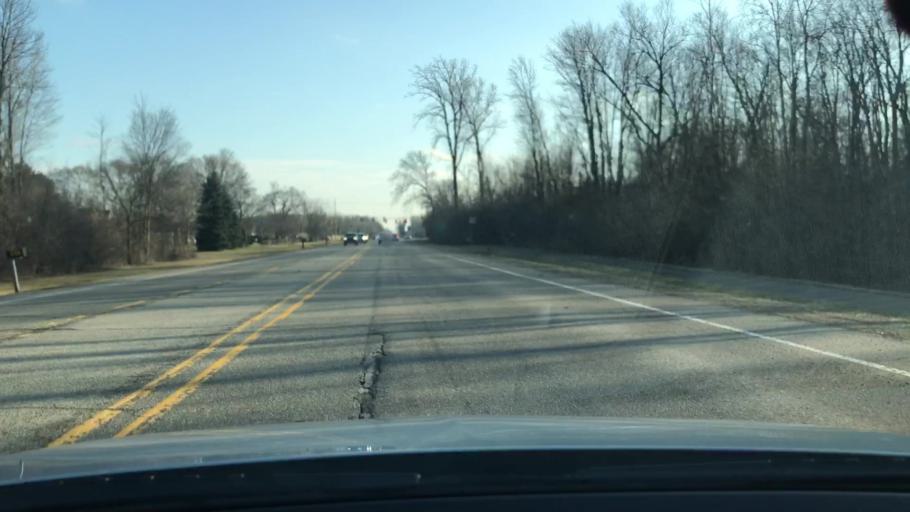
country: US
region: Michigan
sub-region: Oakland County
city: Rochester
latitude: 42.6555
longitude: -83.1127
